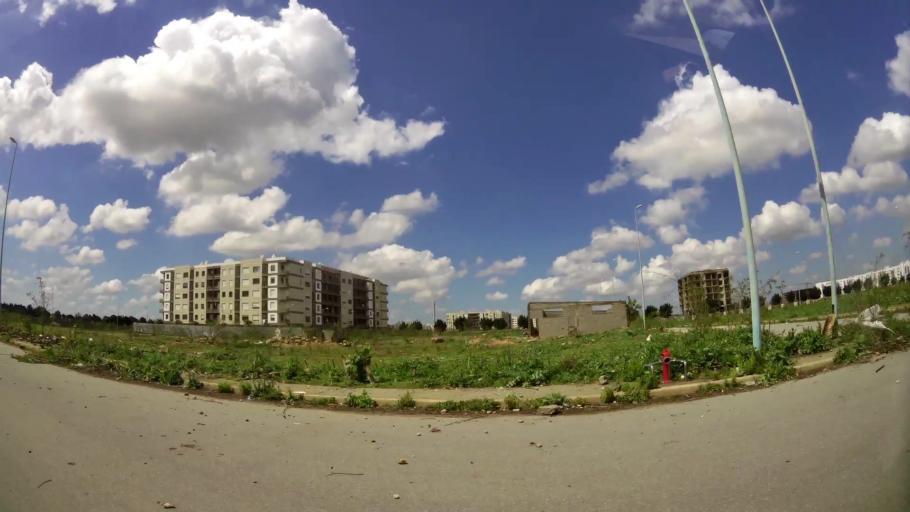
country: MA
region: Chaouia-Ouardigha
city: Nouaseur
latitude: 33.3852
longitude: -7.5577
